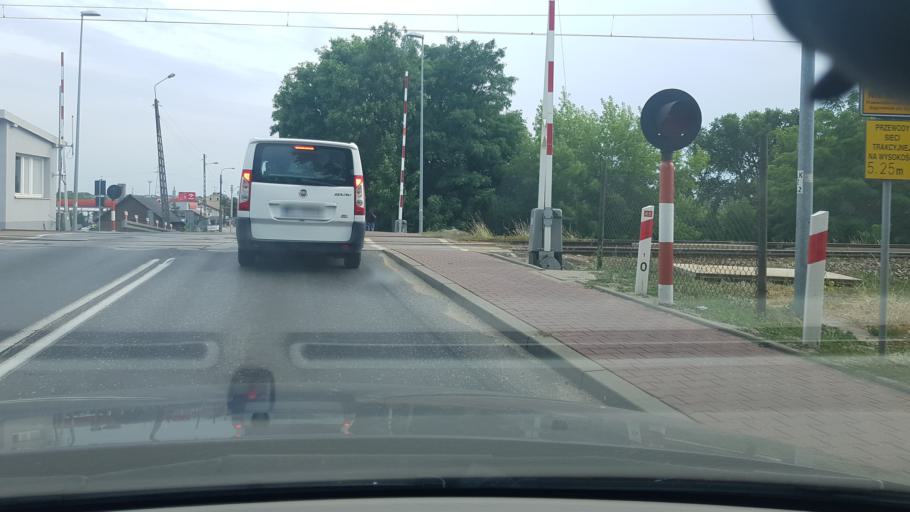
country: PL
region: Lodz Voivodeship
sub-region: Powiat tomaszowski
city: Tomaszow Mazowiecki
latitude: 51.5548
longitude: 20.0181
